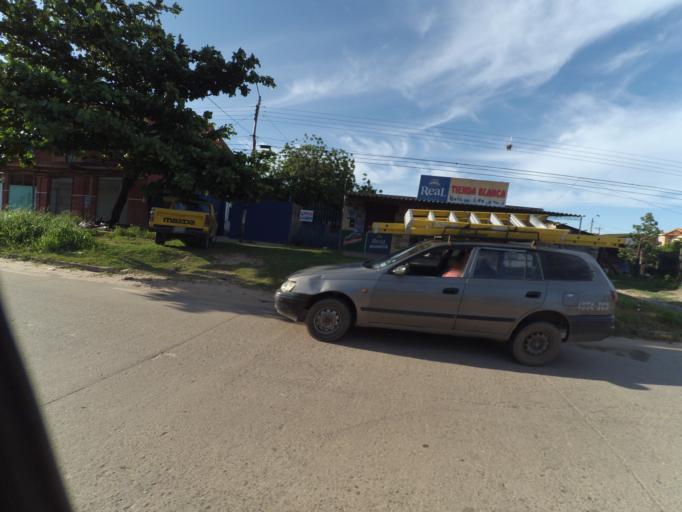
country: BO
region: Santa Cruz
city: Santa Cruz de la Sierra
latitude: -17.7779
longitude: -63.1346
